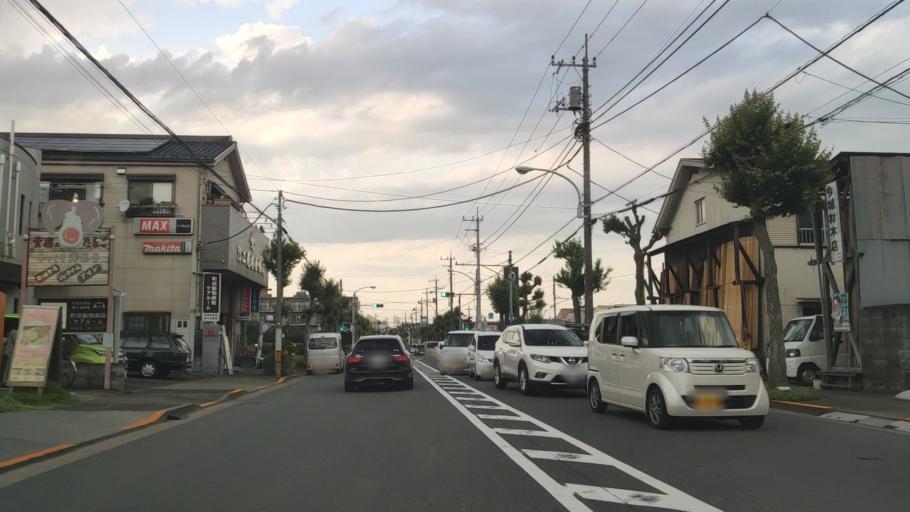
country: JP
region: Tokyo
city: Ome
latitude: 35.7894
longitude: 139.2929
